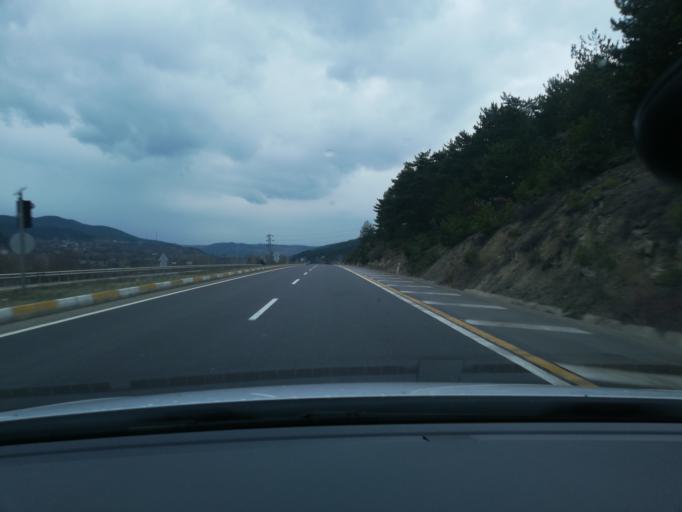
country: TR
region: Bolu
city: Yenicaga
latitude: 40.7457
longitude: 31.8675
